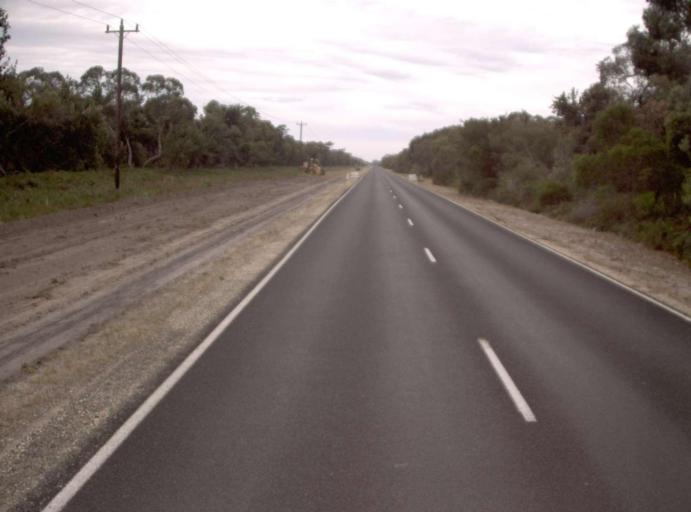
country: AU
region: Victoria
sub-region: East Gippsland
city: Bairnsdale
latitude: -38.0717
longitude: 147.5470
